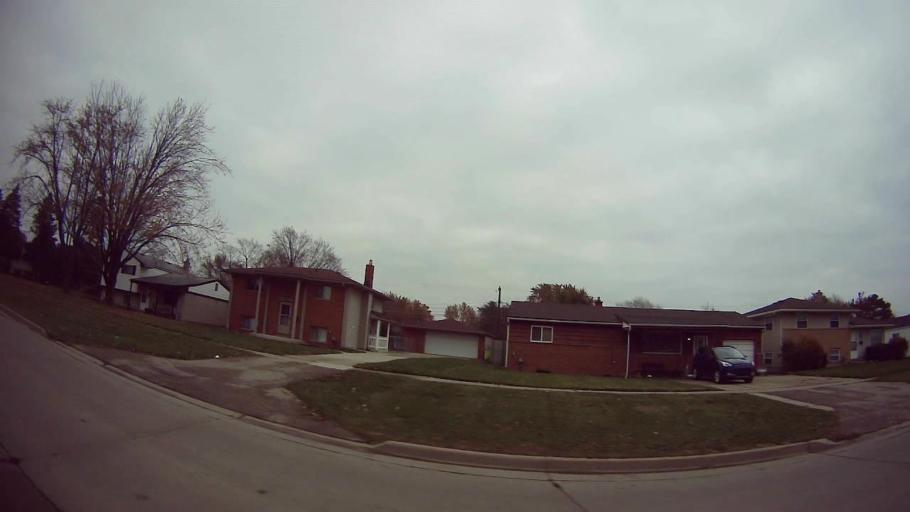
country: US
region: Michigan
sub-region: Oakland County
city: Clawson
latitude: 42.5429
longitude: -83.0875
